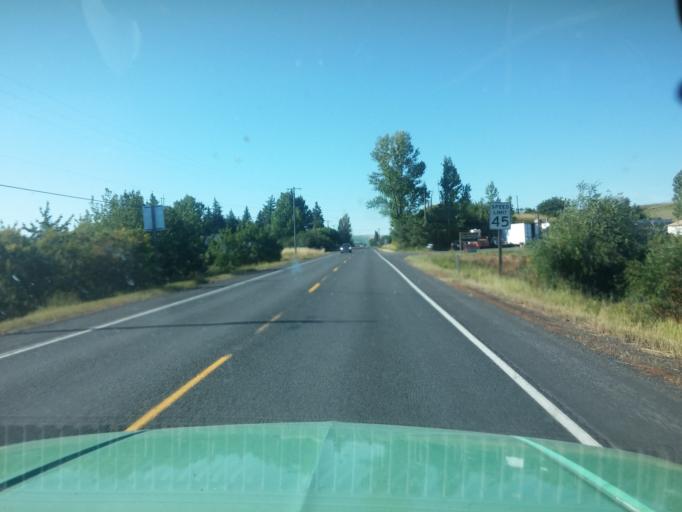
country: US
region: Idaho
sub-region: Latah County
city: Moscow
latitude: 46.7515
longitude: -117.0016
